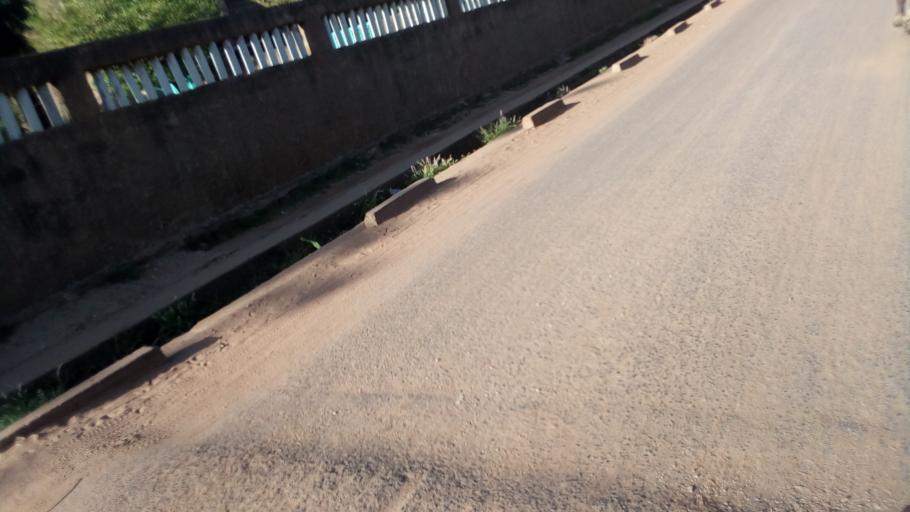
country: ML
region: Kayes
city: Kayes
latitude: 14.4392
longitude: -11.4382
